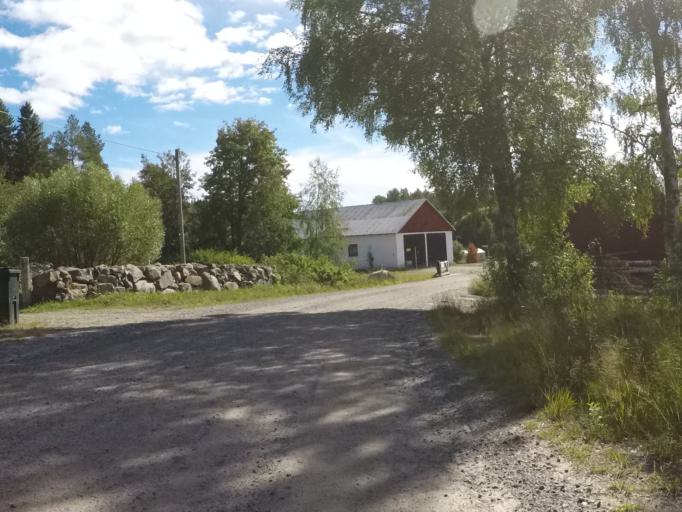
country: SE
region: Vaesterbotten
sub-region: Robertsfors Kommun
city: Robertsfors
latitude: 64.0007
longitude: 20.8111
